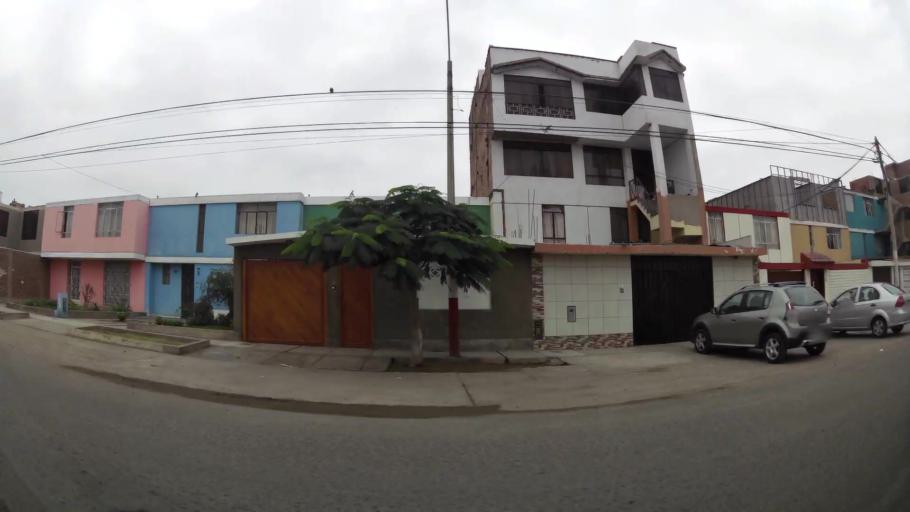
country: PE
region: Callao
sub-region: Callao
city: Callao
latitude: -12.0539
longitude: -77.1079
